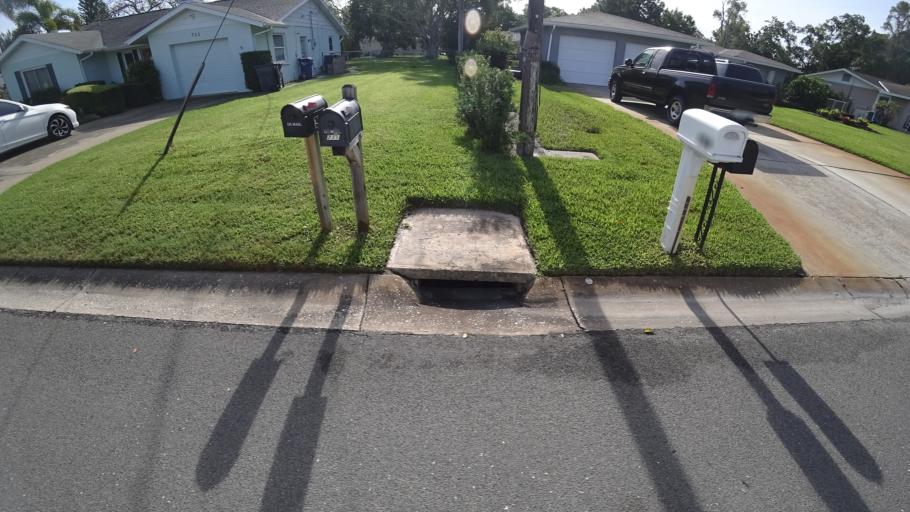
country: US
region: Florida
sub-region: Manatee County
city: West Bradenton
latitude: 27.5054
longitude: -82.6214
